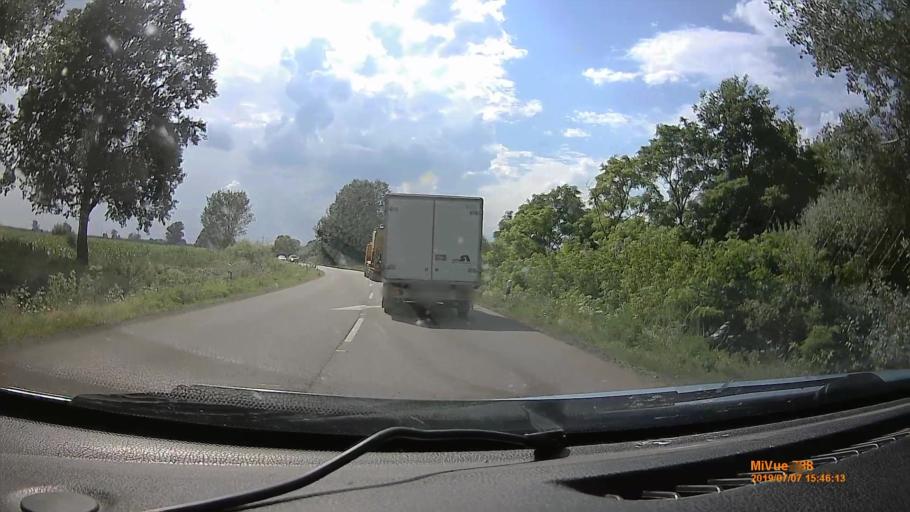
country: HU
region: Jasz-Nagykun-Szolnok
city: Jaszbereny
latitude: 47.5183
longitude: 19.8968
